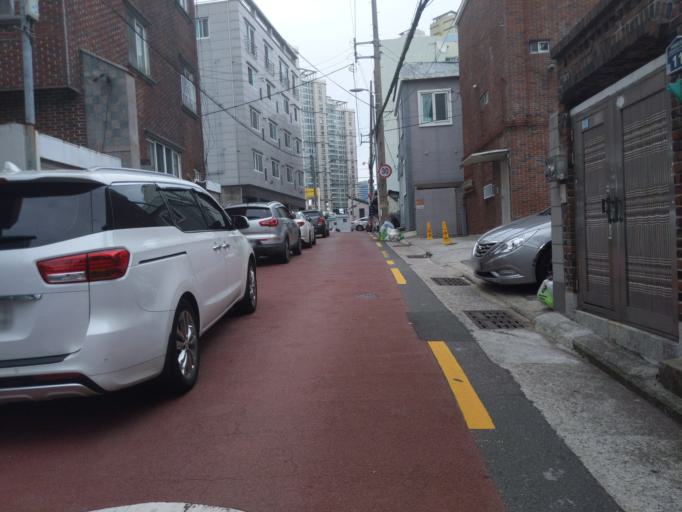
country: KR
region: Busan
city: Busan
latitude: 35.1590
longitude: 129.1280
